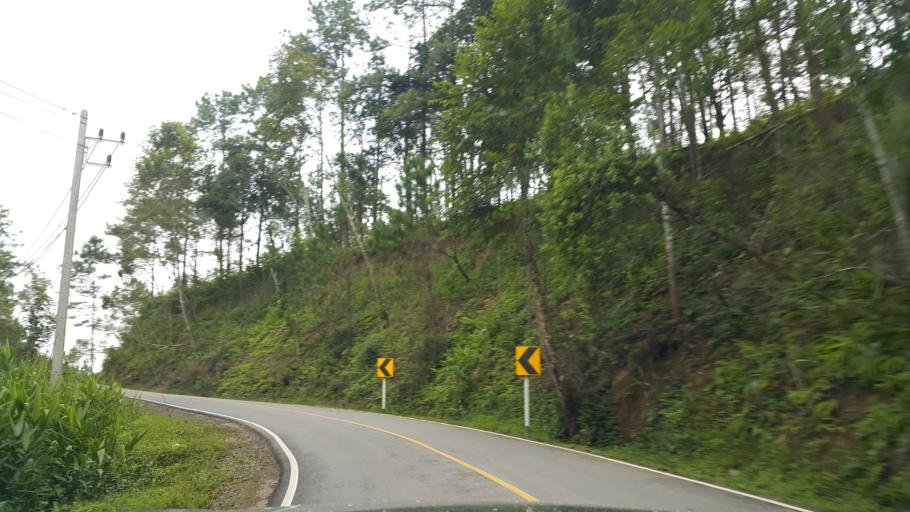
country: TH
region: Chiang Mai
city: Samoeng
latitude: 18.8870
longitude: 98.4989
